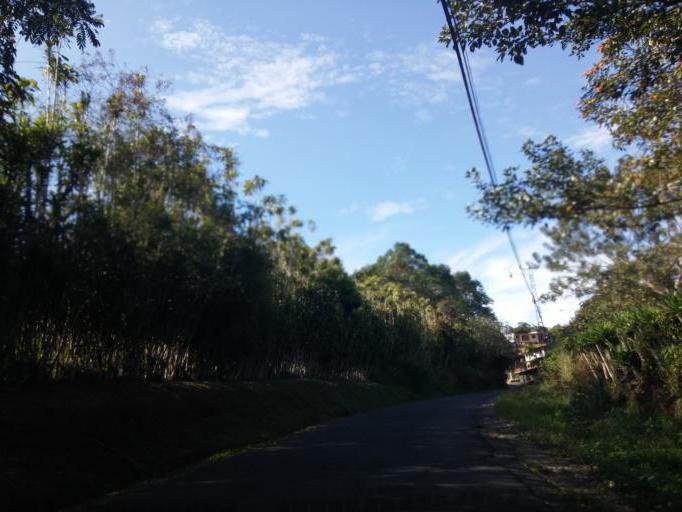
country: CR
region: Alajuela
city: Alajuela
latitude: 10.0368
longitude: -84.2068
